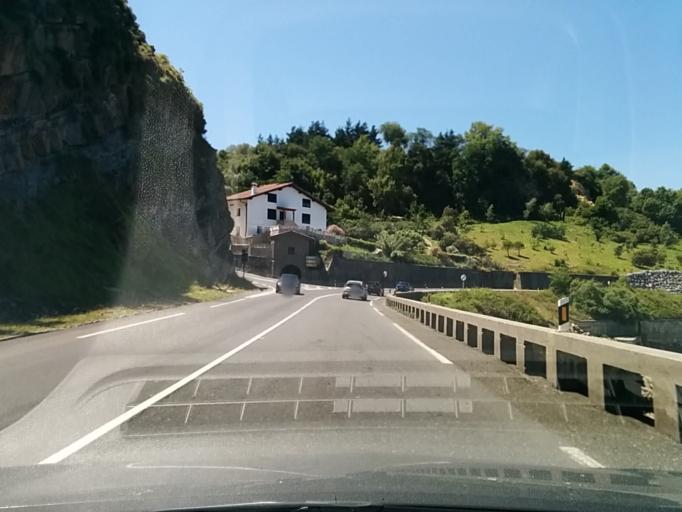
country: ES
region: Basque Country
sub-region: Provincia de Guipuzcoa
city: Getaria
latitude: 43.3069
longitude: -2.2131
